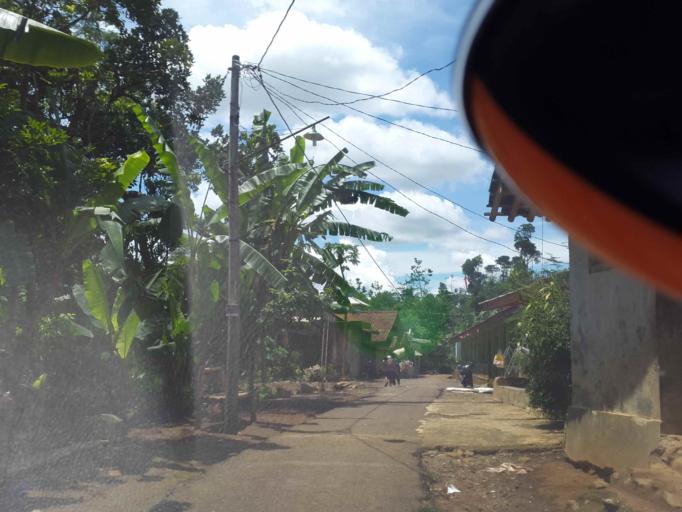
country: ID
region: Central Java
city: Purbalingga
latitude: -7.3543
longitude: 109.6213
